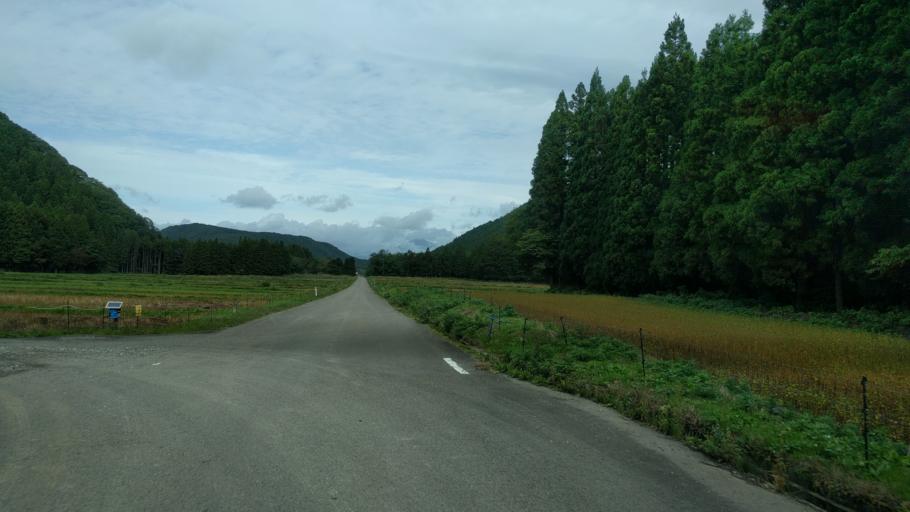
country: JP
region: Fukushima
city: Inawashiro
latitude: 37.3820
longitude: 140.1520
